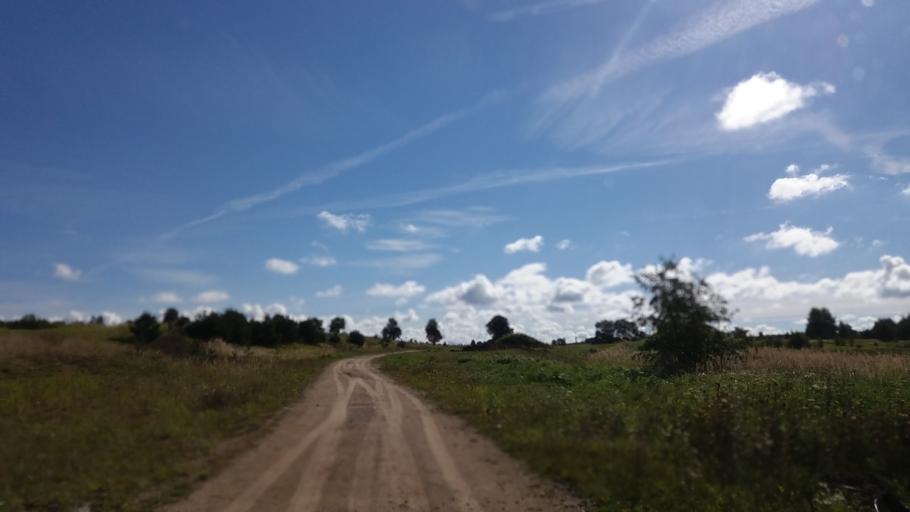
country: PL
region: West Pomeranian Voivodeship
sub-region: Powiat choszczenski
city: Krzecin
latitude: 53.1306
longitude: 15.4960
